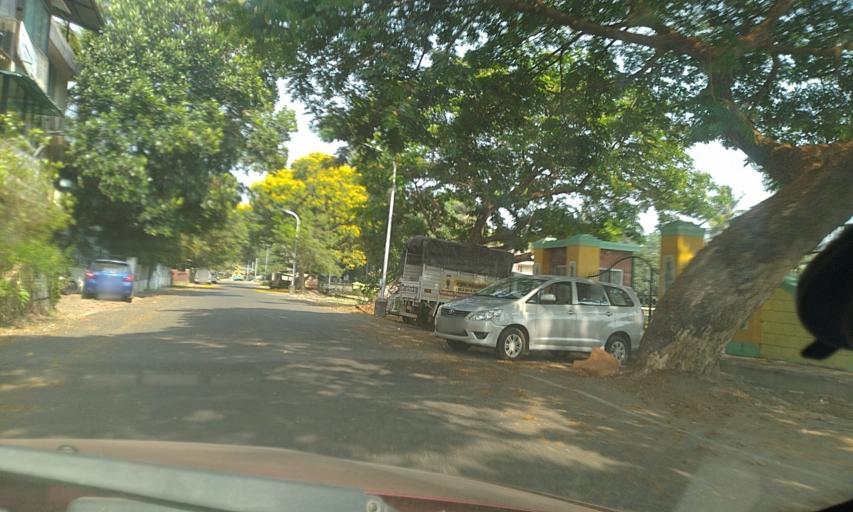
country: IN
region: Goa
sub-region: North Goa
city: Panaji
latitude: 15.4853
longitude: 73.8142
